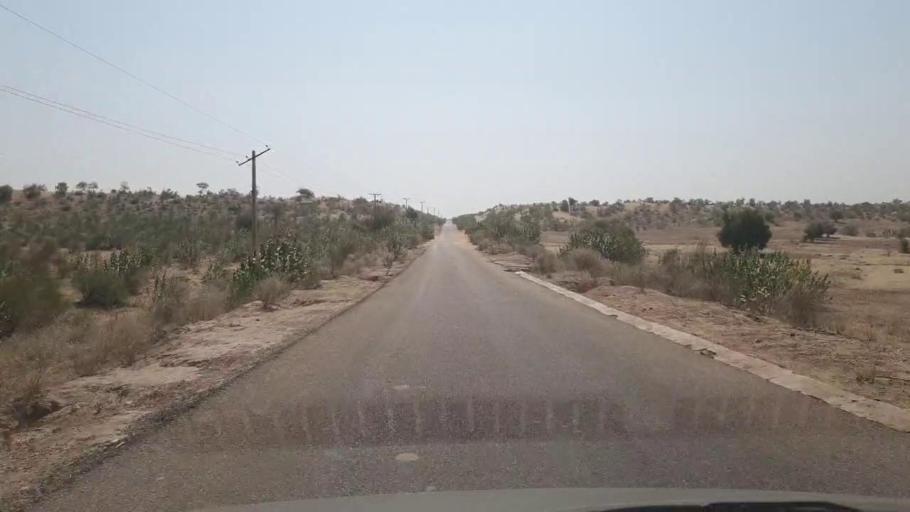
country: PK
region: Sindh
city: Chor
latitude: 25.6280
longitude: 70.1744
